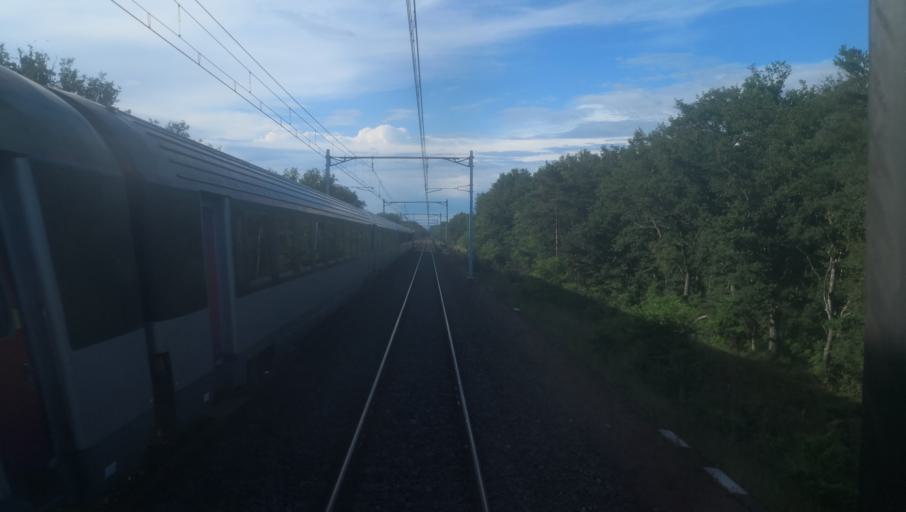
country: FR
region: Centre
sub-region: Departement du Loir-et-Cher
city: Theillay
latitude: 47.3336
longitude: 2.0462
